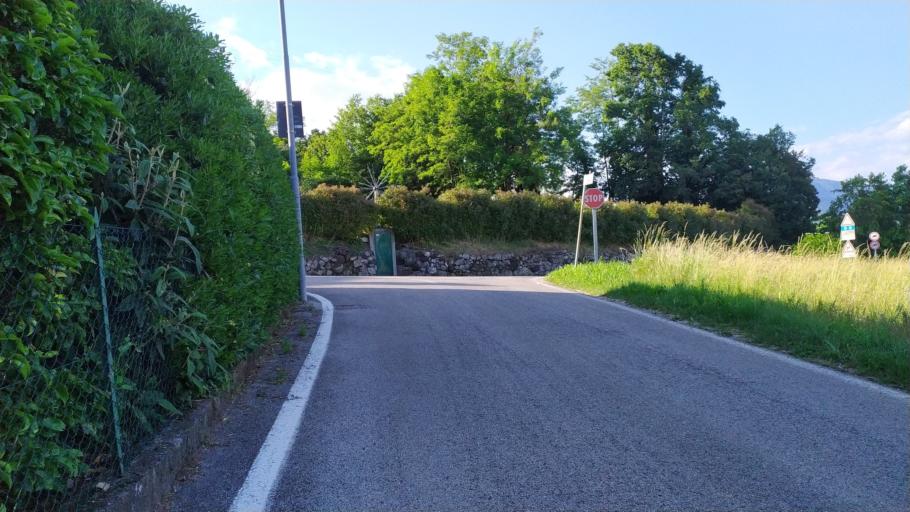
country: IT
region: Veneto
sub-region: Provincia di Vicenza
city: Schio
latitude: 45.6875
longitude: 11.3390
